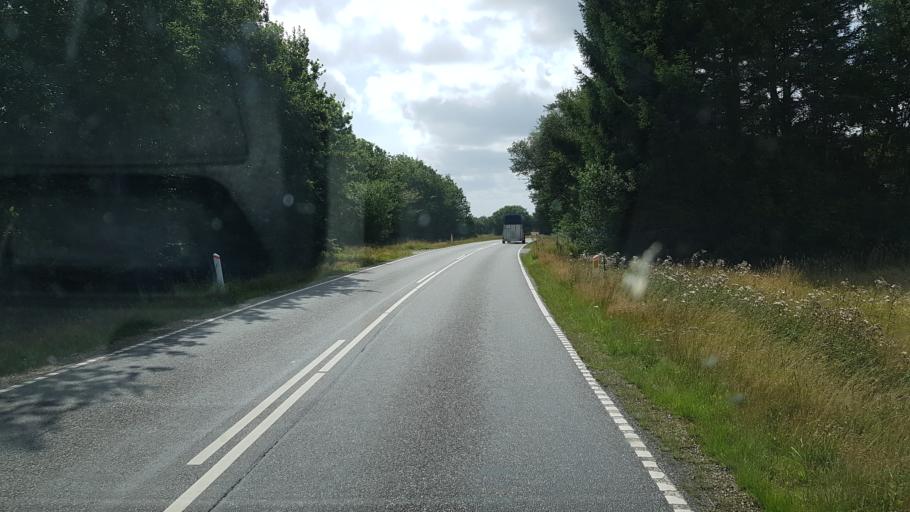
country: DK
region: South Denmark
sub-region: Vejen Kommune
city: Brorup
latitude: 55.5307
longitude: 9.0486
